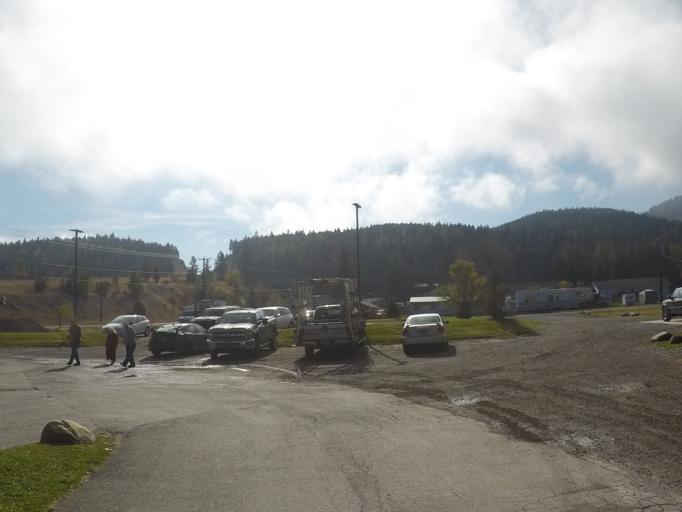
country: US
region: Montana
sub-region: Flathead County
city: Lakeside
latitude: 48.0158
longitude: -114.2255
